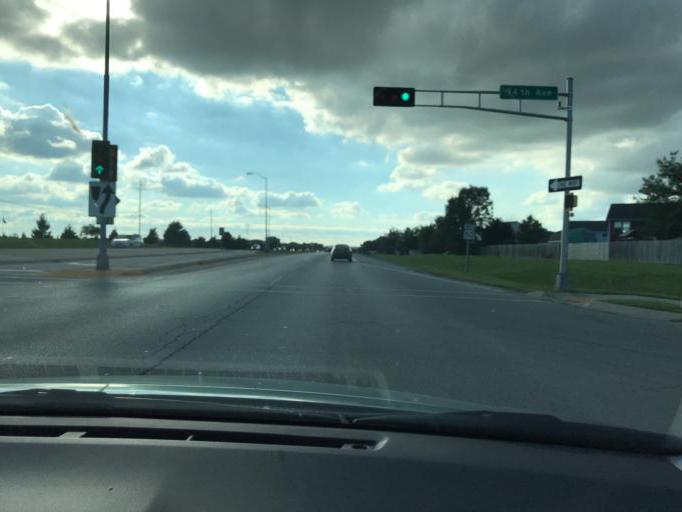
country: US
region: Wisconsin
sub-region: Kenosha County
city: Pleasant Prairie
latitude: 42.5668
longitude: -87.9211
